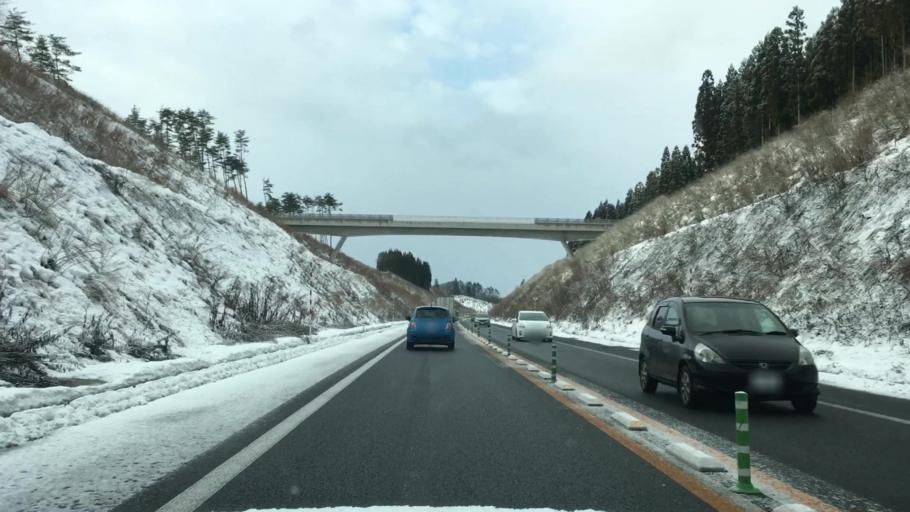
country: JP
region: Akita
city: Takanosu
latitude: 40.2154
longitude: 140.4220
